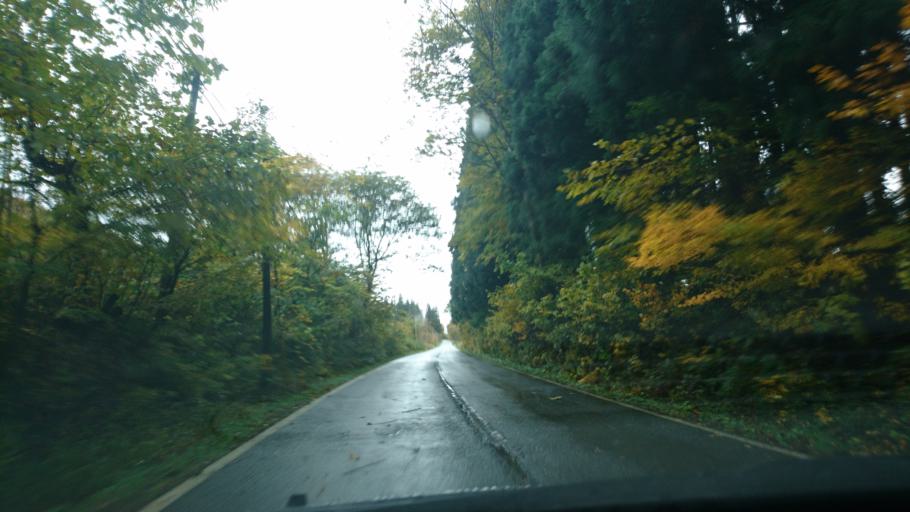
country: JP
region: Iwate
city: Shizukuishi
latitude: 39.6162
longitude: 140.9446
